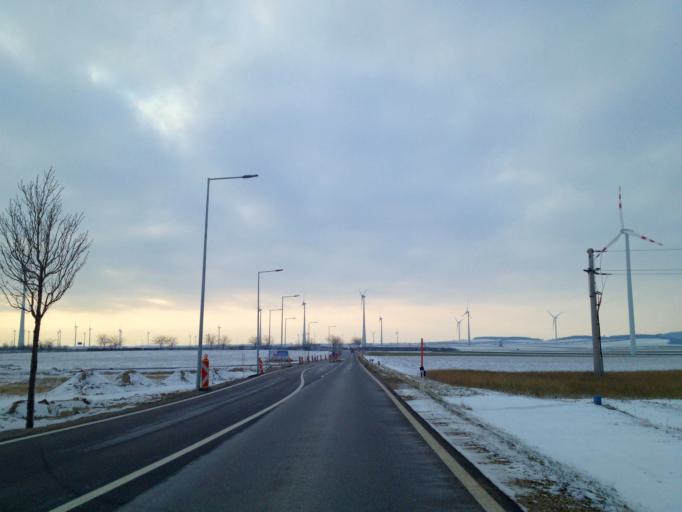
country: AT
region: Lower Austria
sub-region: Politischer Bezirk Bruck an der Leitha
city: Berg
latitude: 48.0855
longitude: 17.0439
